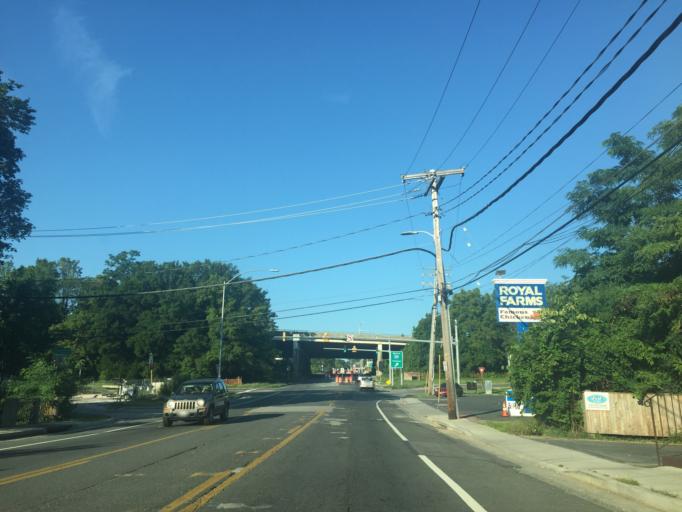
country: US
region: Maryland
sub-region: Baltimore County
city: Catonsville
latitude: 39.2807
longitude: -76.7259
